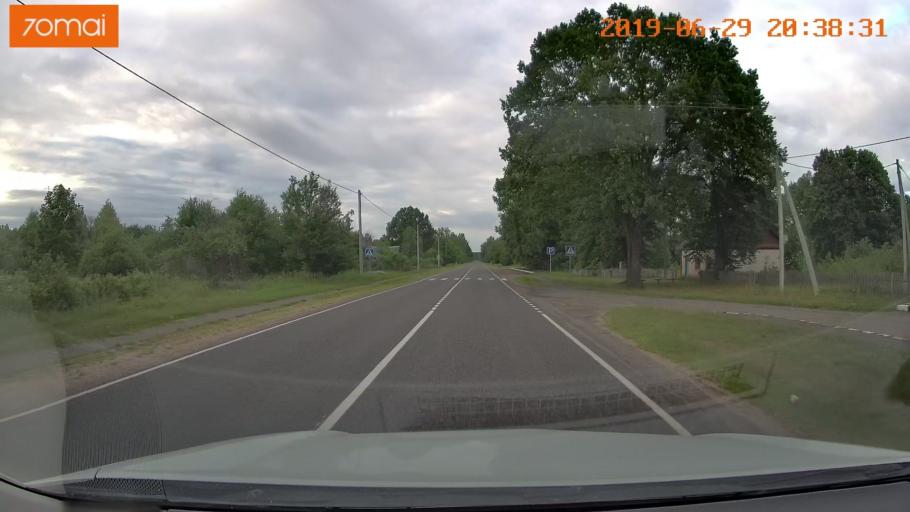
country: BY
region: Brest
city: Hantsavichy
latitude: 52.5509
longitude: 26.3645
